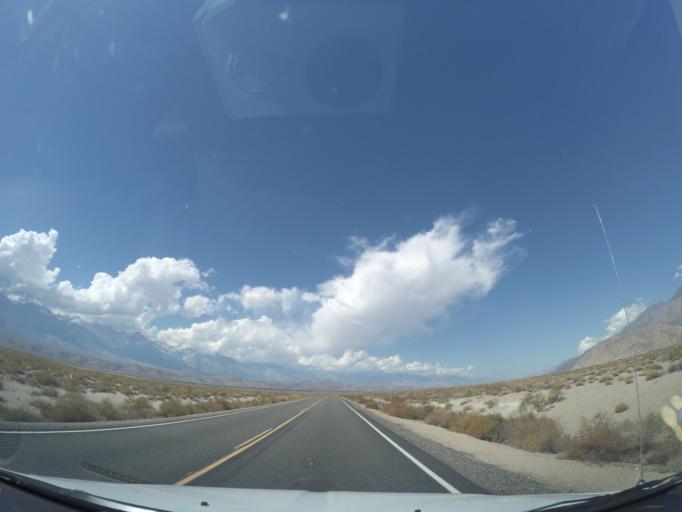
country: US
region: California
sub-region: Inyo County
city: Lone Pine
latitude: 36.5715
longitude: -117.9902
